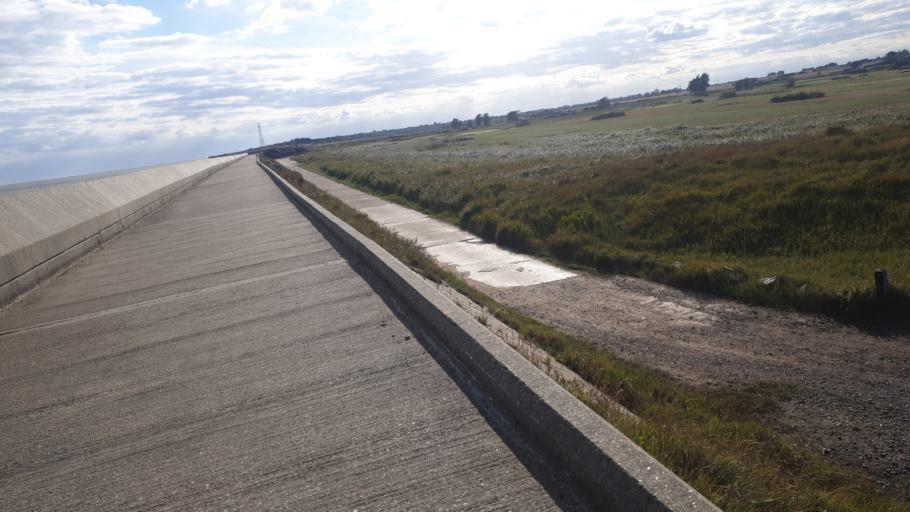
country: GB
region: England
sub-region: Essex
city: Frinton-on-Sea
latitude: 51.8192
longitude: 1.2362
